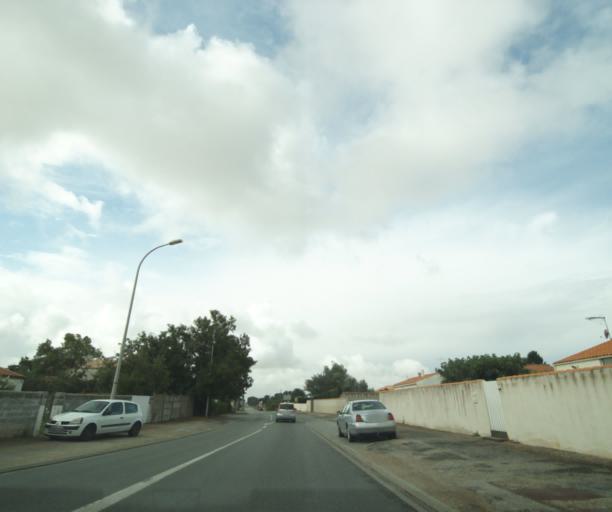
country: FR
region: Poitou-Charentes
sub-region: Departement de la Charente-Maritime
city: Charron
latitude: 46.3050
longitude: -1.0879
